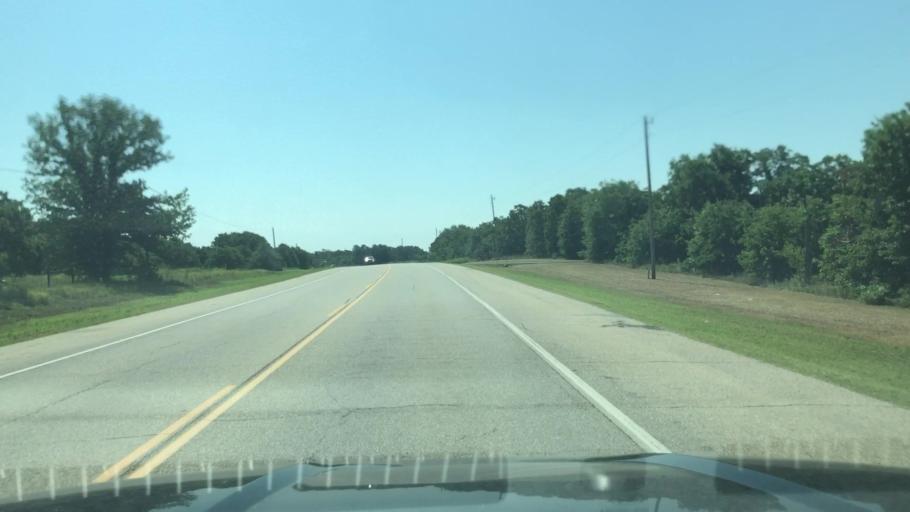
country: US
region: Oklahoma
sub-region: Creek County
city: Mannford
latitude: 35.9918
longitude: -96.3530
